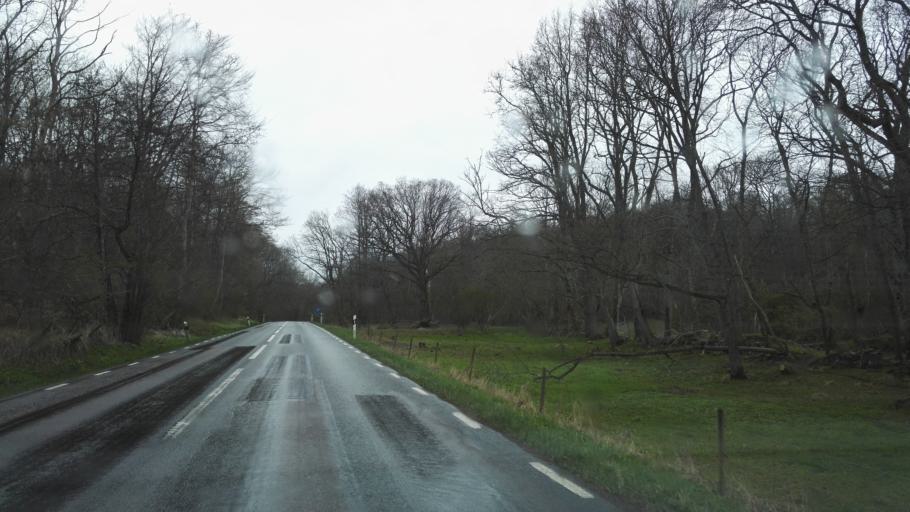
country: SE
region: Skane
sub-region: Simrishamns Kommun
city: Kivik
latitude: 55.6536
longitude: 14.2190
